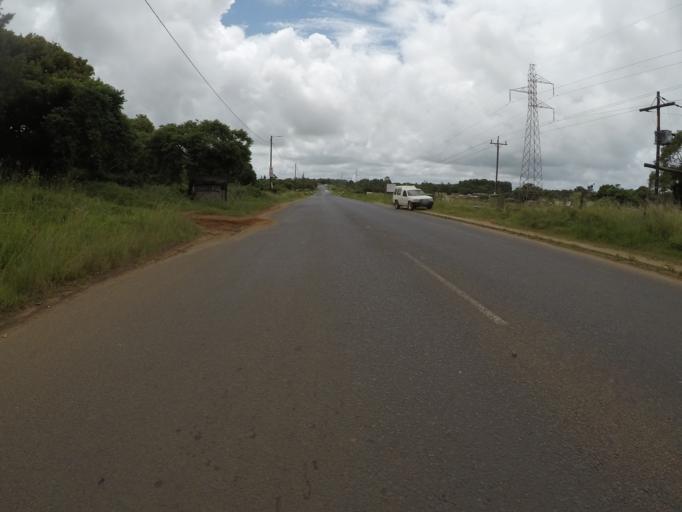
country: ZA
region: KwaZulu-Natal
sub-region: uThungulu District Municipality
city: eSikhawini
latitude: -28.8318
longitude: 31.9408
